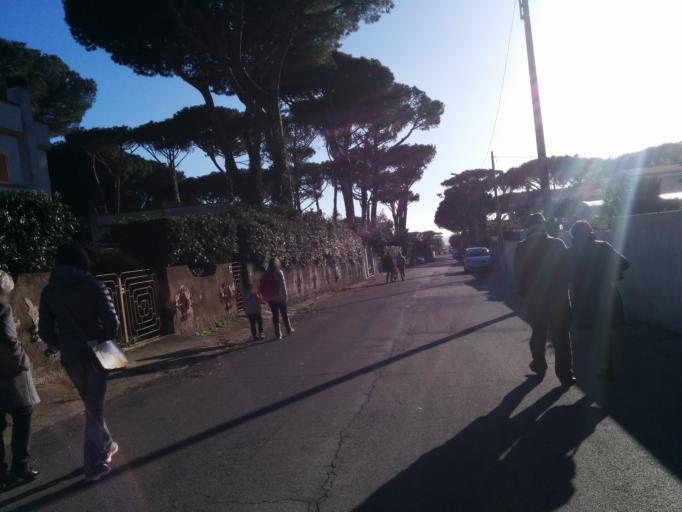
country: IT
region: Latium
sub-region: Citta metropolitana di Roma Capitale
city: Lavinio
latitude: 41.4998
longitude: 12.5948
